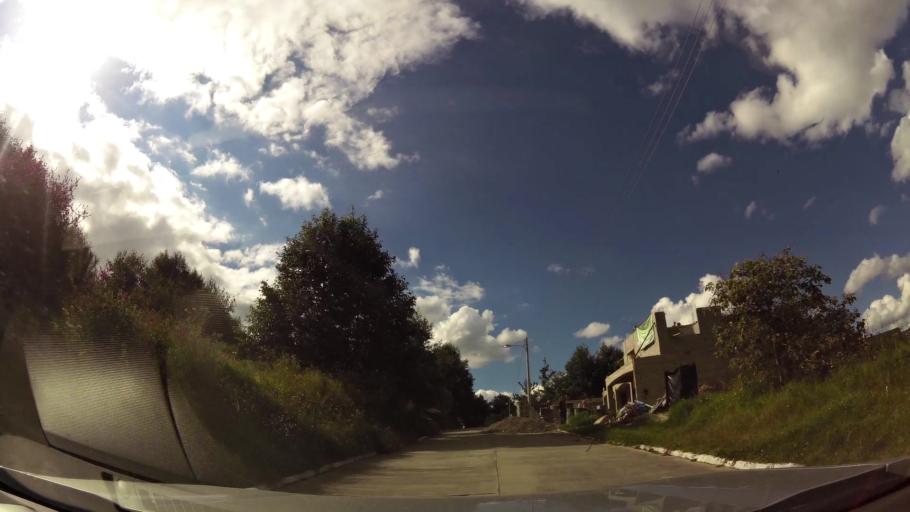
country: GT
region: Quetzaltenango
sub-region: Municipio de La Esperanza
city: La Esperanza
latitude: 14.8346
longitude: -91.5598
